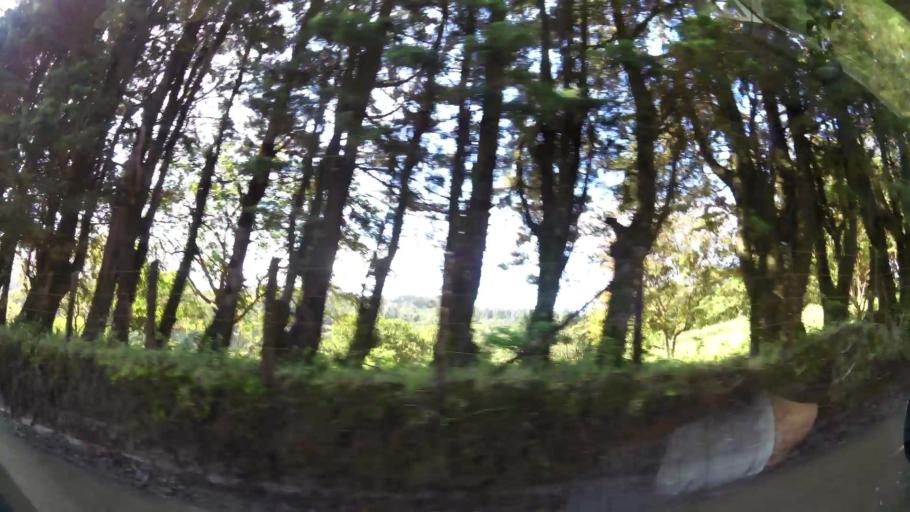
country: CR
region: Guanacaste
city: Juntas
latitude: 10.3255
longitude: -84.8263
